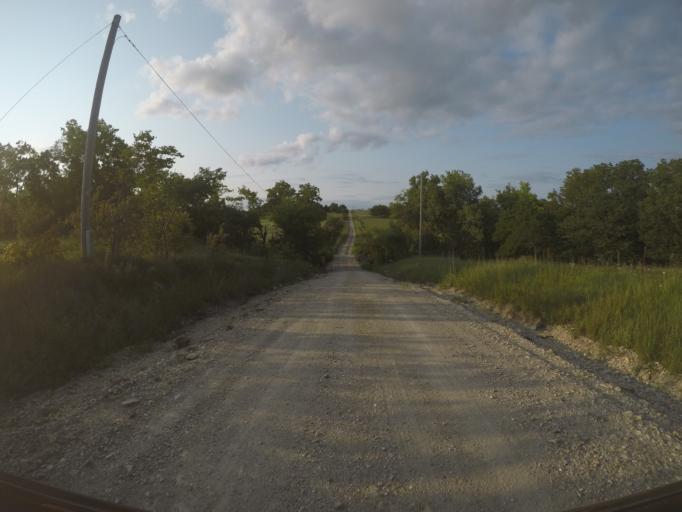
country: US
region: Kansas
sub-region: Wabaunsee County
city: Alma
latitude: 39.0733
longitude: -96.3773
